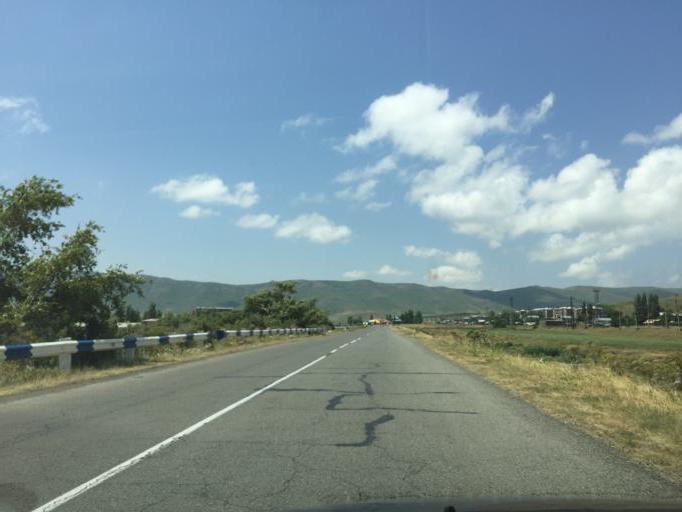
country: AM
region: Geghark'unik'i Marz
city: Tsovagyugh
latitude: 40.6313
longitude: 44.9810
